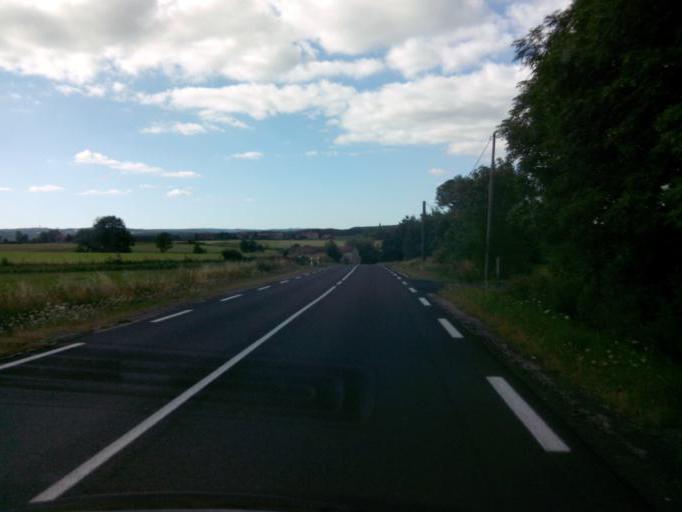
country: FR
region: Auvergne
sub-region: Departement de la Haute-Loire
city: Saint-Paulien
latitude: 45.1875
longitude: 3.8241
